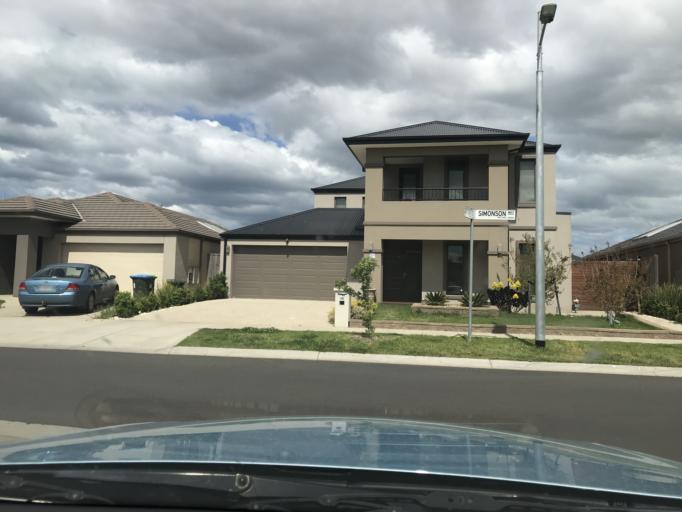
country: AU
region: Victoria
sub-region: Wyndham
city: Williams Landing
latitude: -37.8584
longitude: 144.7547
